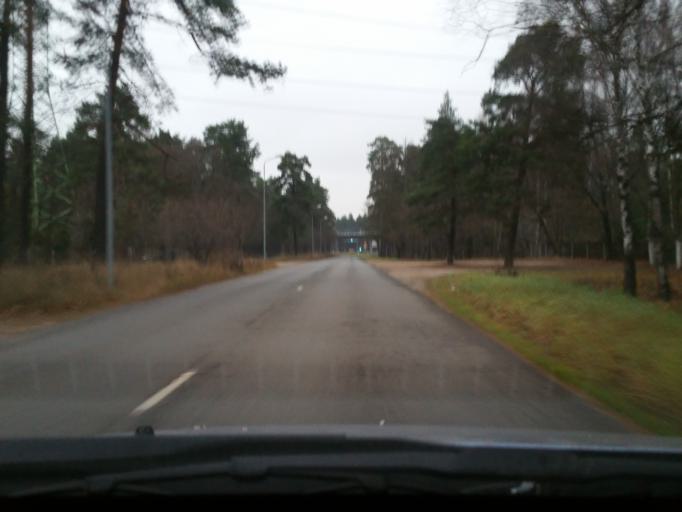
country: LV
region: Riga
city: Jaunciems
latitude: 56.9932
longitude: 24.1406
